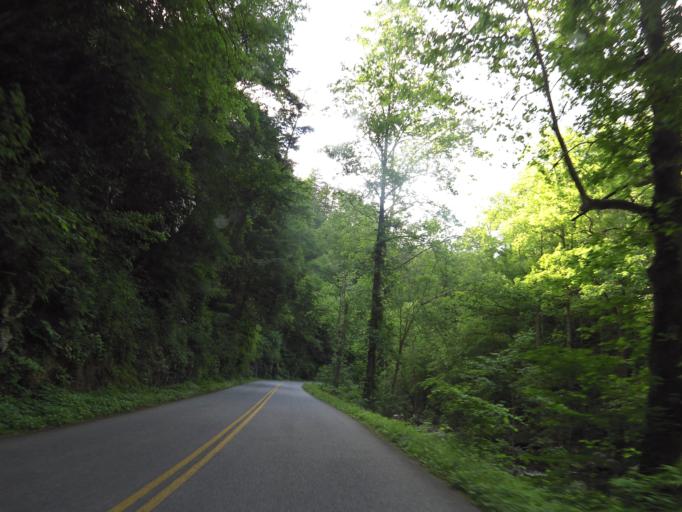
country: US
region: Tennessee
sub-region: Sevier County
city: Pigeon Forge
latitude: 35.6728
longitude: -83.6917
